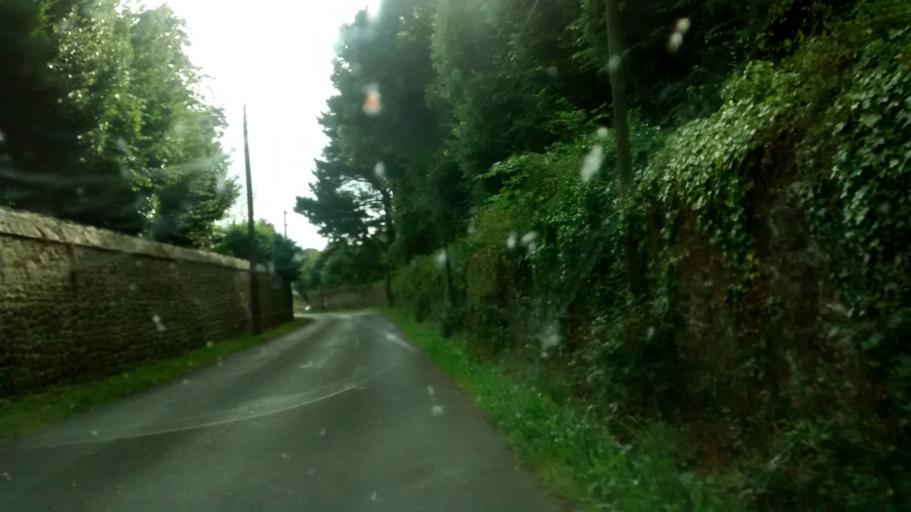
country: FR
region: Brittany
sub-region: Departement d'Ille-et-Vilaine
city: La Gouesniere
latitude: 48.5987
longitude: -1.8926
